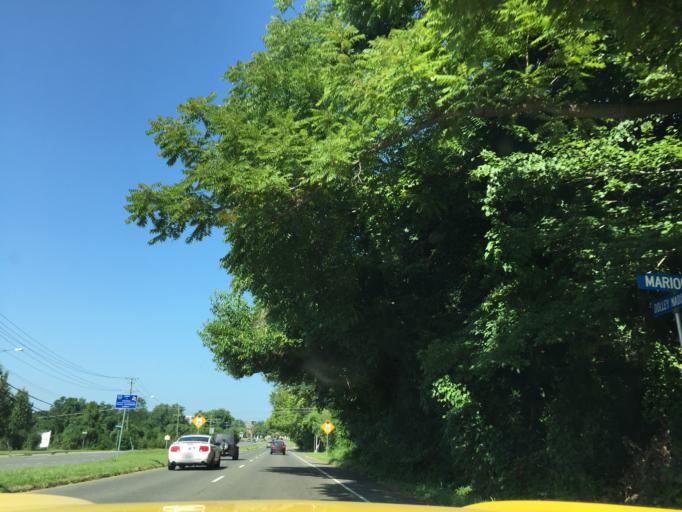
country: US
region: Virginia
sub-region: Fairfax County
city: McLean
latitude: 38.9423
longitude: -77.1687
